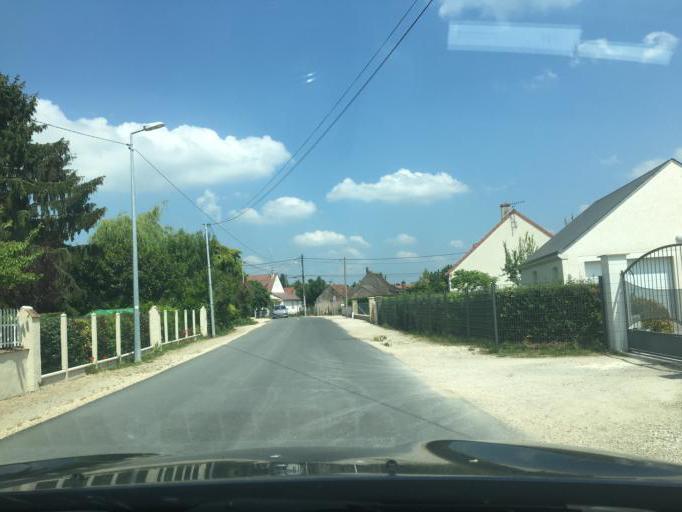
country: FR
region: Centre
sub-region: Departement du Loiret
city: Trainou
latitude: 47.9773
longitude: 2.1078
